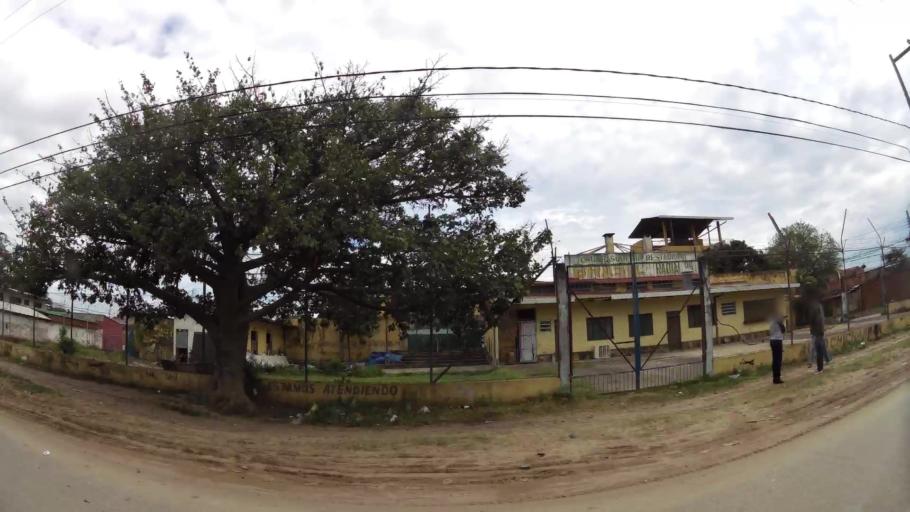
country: BO
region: Santa Cruz
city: Santa Cruz de la Sierra
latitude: -17.7263
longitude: -63.1791
